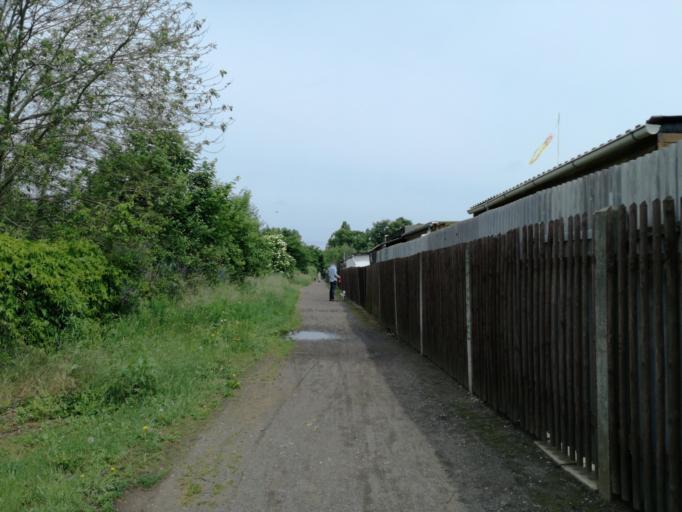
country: DE
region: Saxony
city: Leipzig
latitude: 51.3883
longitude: 12.3185
